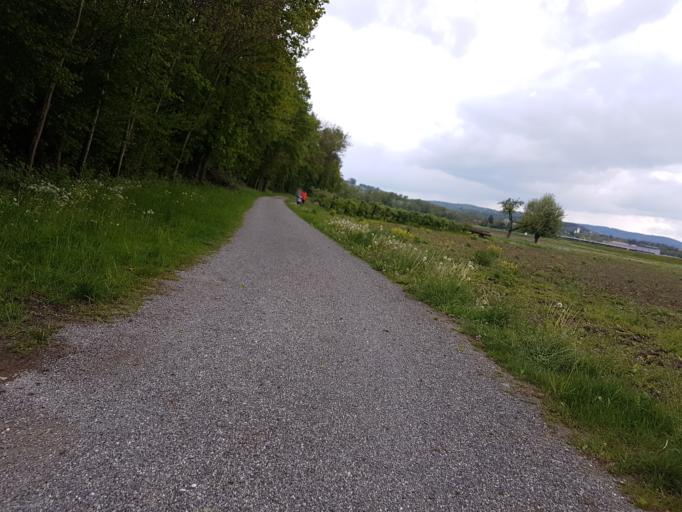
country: CH
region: Aargau
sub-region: Bezirk Brugg
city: Lauffohr (Brugg)
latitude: 47.5003
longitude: 8.2329
